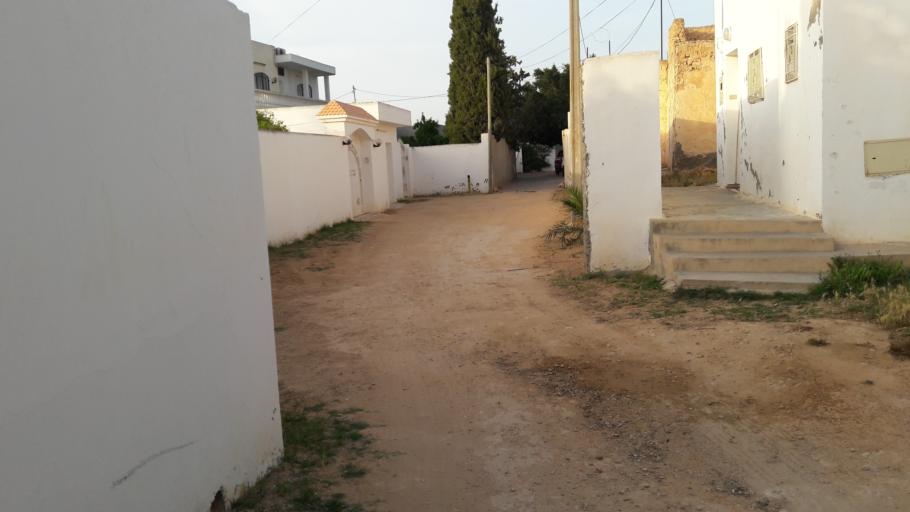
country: TN
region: Safaqis
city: Al Qarmadah
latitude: 34.8153
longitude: 10.7468
